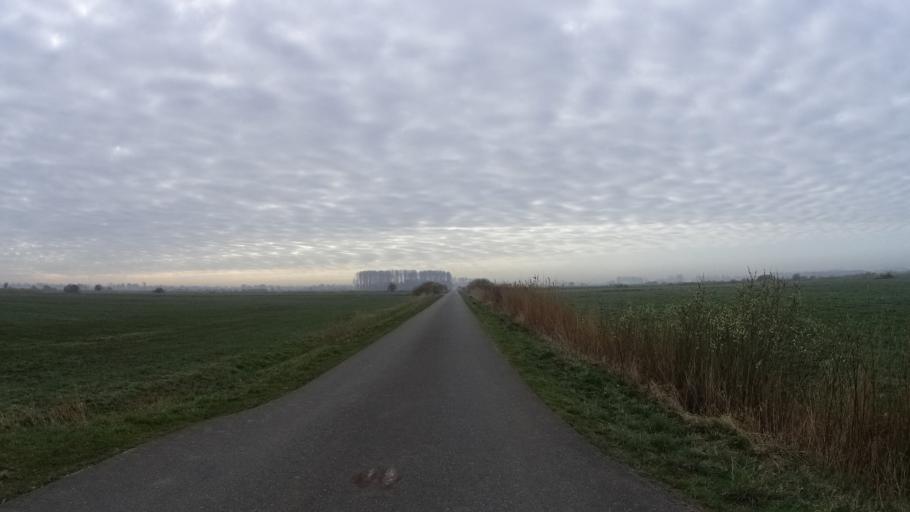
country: DE
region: Lower Saxony
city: Upgant-Schott
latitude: 53.4620
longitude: 7.3198
